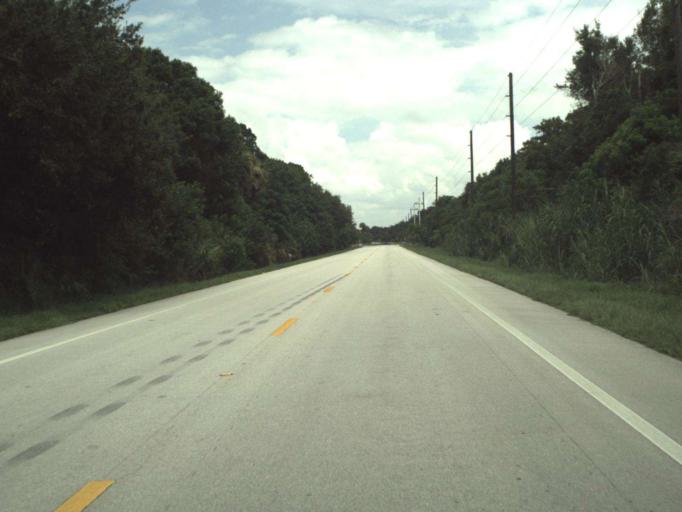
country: US
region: Florida
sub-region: Okeechobee County
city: Taylor Creek
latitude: 27.1041
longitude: -80.6597
